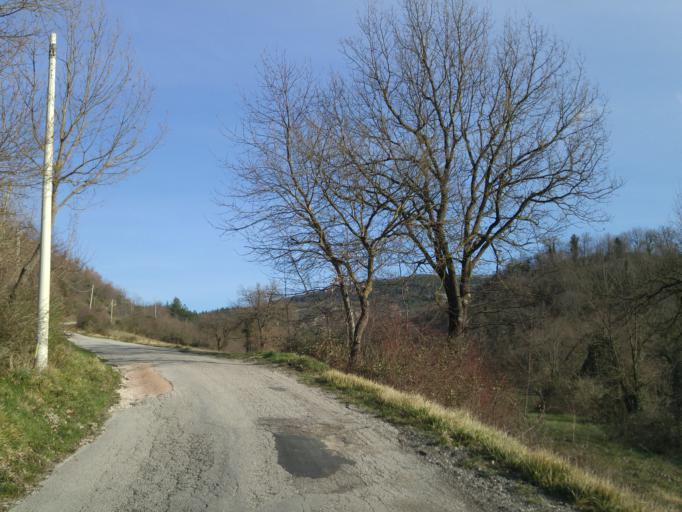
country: IT
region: The Marches
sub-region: Provincia di Pesaro e Urbino
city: Fermignano
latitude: 43.6786
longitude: 12.6667
